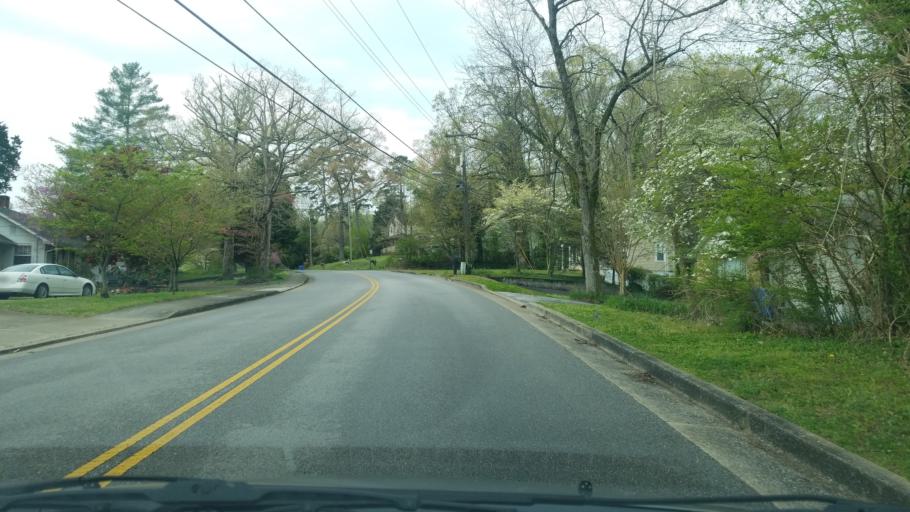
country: US
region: Tennessee
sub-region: Hamilton County
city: Collegedale
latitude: 35.0419
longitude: -85.0549
